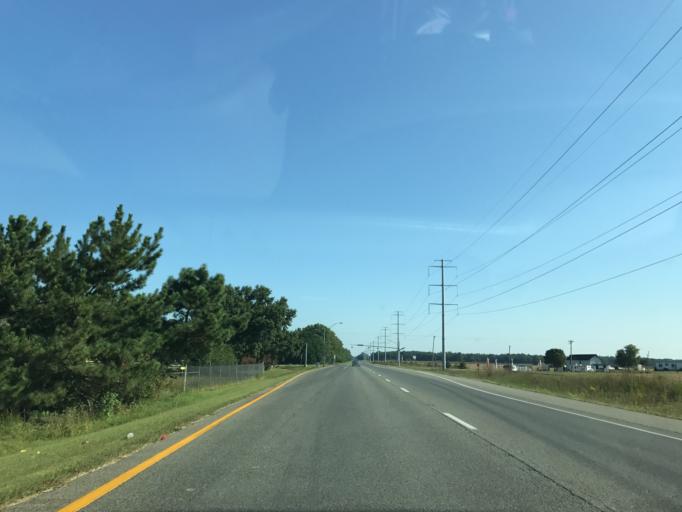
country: US
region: Maryland
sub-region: Queen Anne's County
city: Centreville
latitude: 39.0773
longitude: -75.9790
